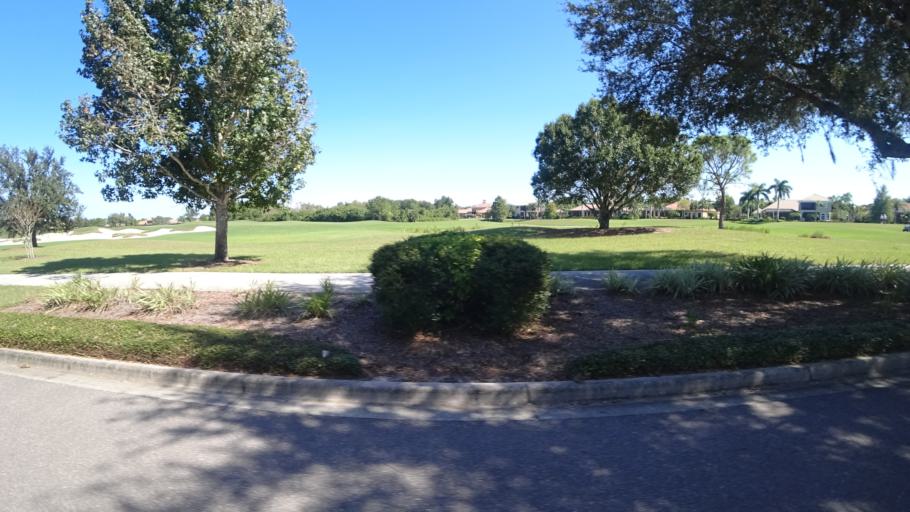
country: US
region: Florida
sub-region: Sarasota County
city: The Meadows
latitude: 27.3997
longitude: -82.4108
